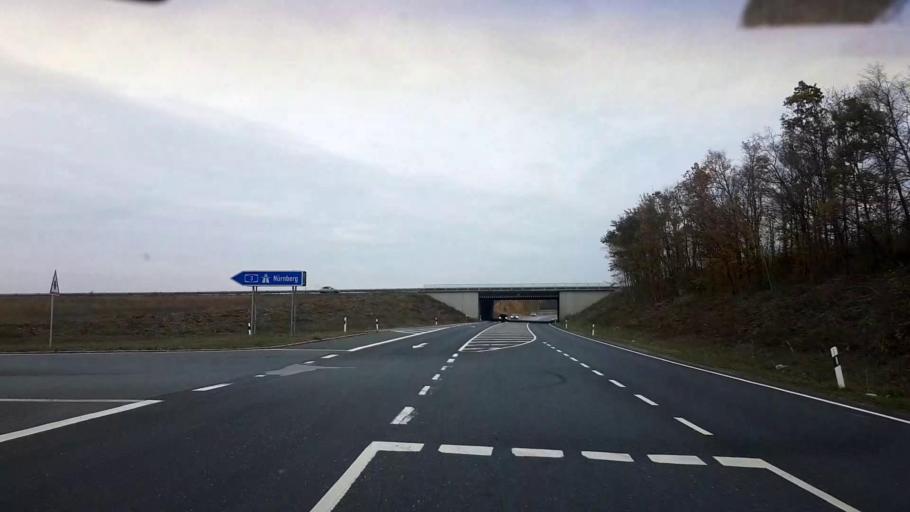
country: DE
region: Bavaria
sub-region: Regierungsbezirk Unterfranken
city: Wiesentheid
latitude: 49.7737
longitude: 10.3460
